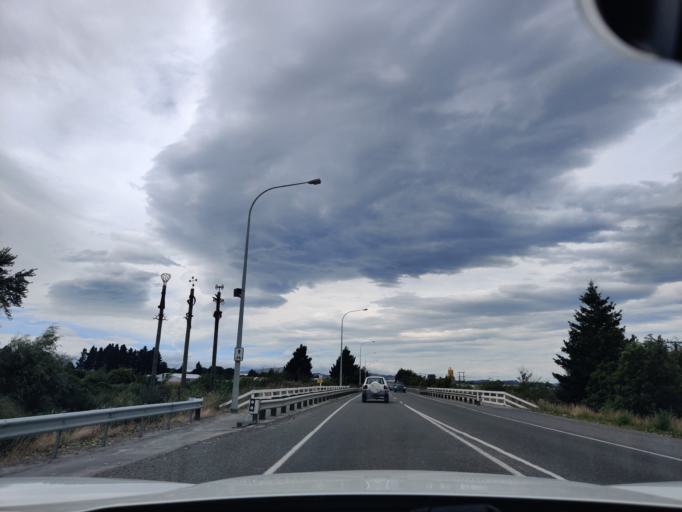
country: NZ
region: Wellington
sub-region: Masterton District
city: Masterton
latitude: -40.9654
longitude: 175.6081
